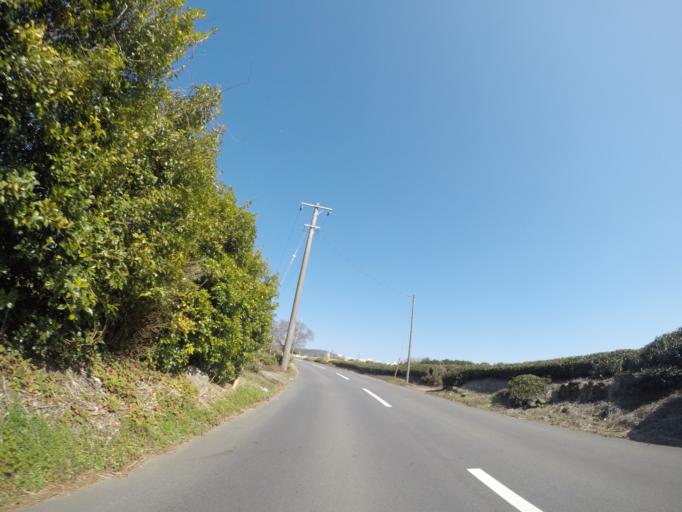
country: JP
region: Shizuoka
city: Numazu
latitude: 35.1441
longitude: 138.8225
